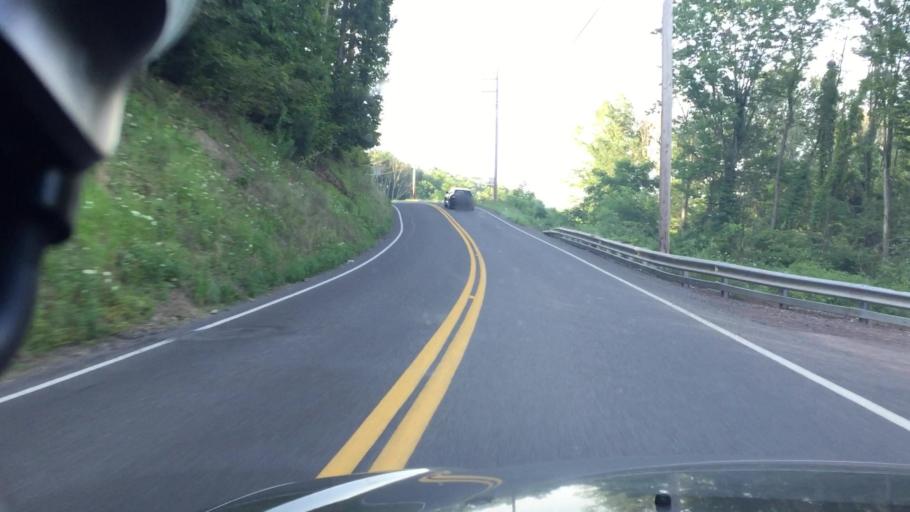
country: US
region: Pennsylvania
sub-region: Columbia County
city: Mifflinville
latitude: 41.0117
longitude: -76.3178
